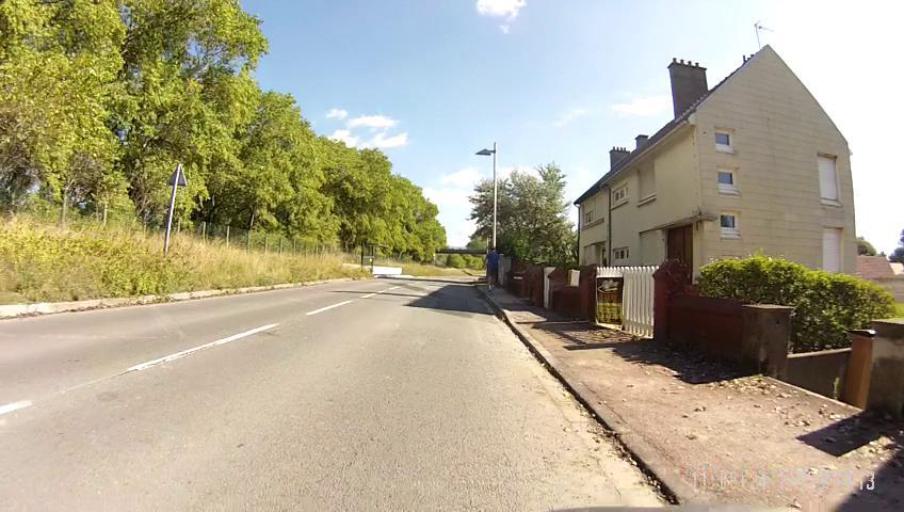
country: FR
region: Nord-Pas-de-Calais
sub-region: Departement du Nord
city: Bray-Dunes
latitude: 51.0690
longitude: 2.5096
